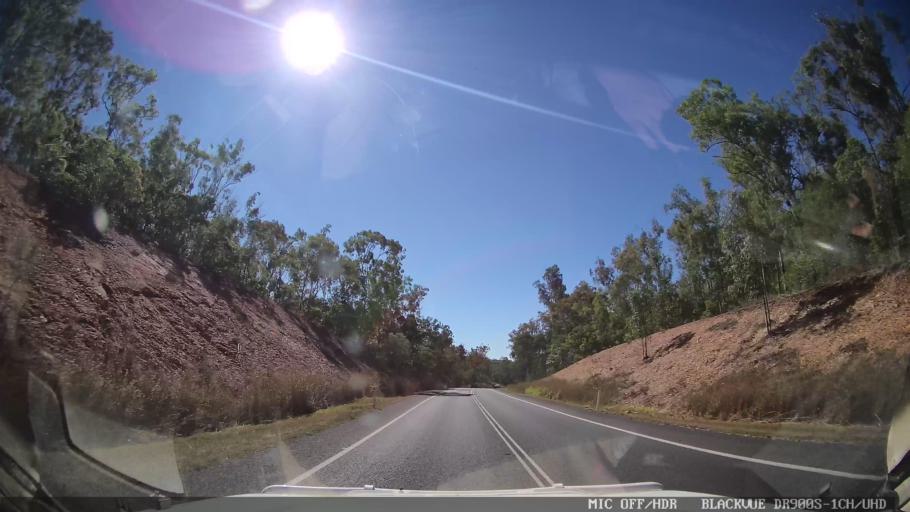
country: AU
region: Queensland
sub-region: Gladstone
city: Toolooa
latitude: -23.9646
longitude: 151.2175
